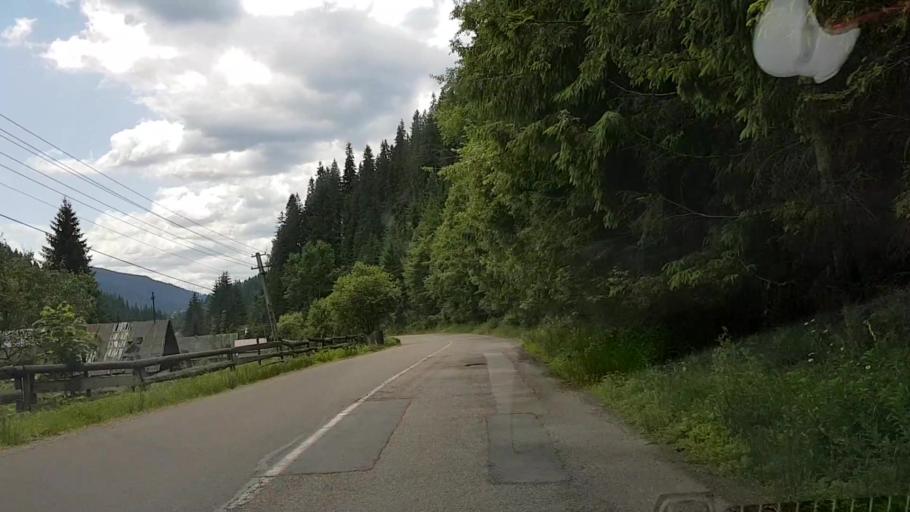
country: RO
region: Suceava
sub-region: Comuna Crucea
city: Crucea
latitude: 47.3489
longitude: 25.6058
